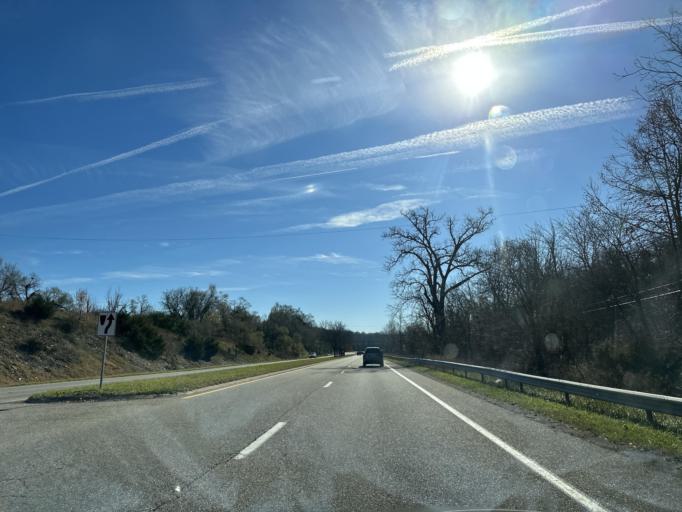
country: US
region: Virginia
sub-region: Augusta County
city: Jolivue
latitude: 38.1183
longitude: -79.0200
